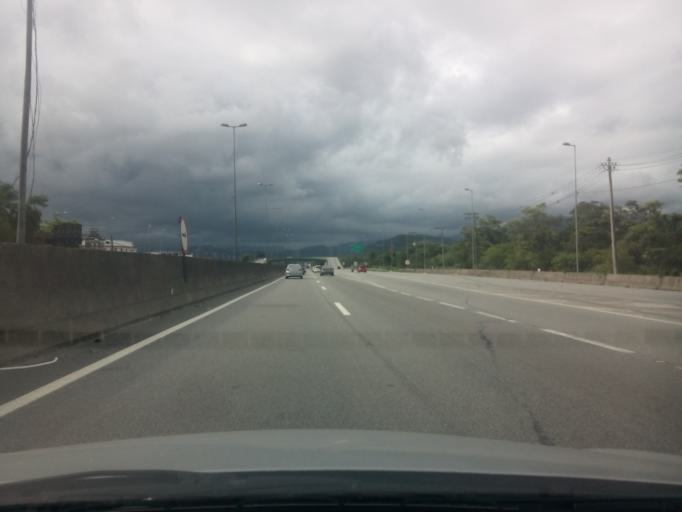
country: BR
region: Sao Paulo
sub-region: Santos
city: Santos
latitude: -23.9402
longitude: -46.2807
